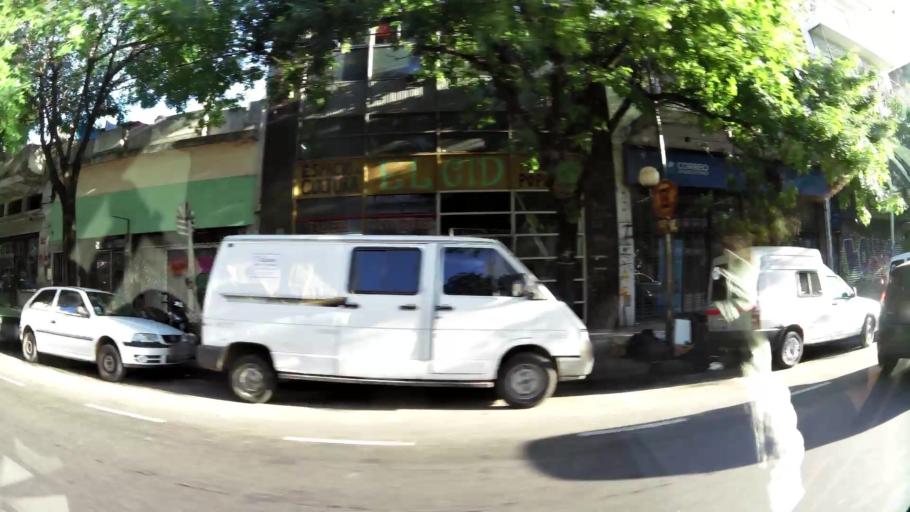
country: AR
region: Buenos Aires F.D.
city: Colegiales
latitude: -34.6061
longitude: -58.4409
